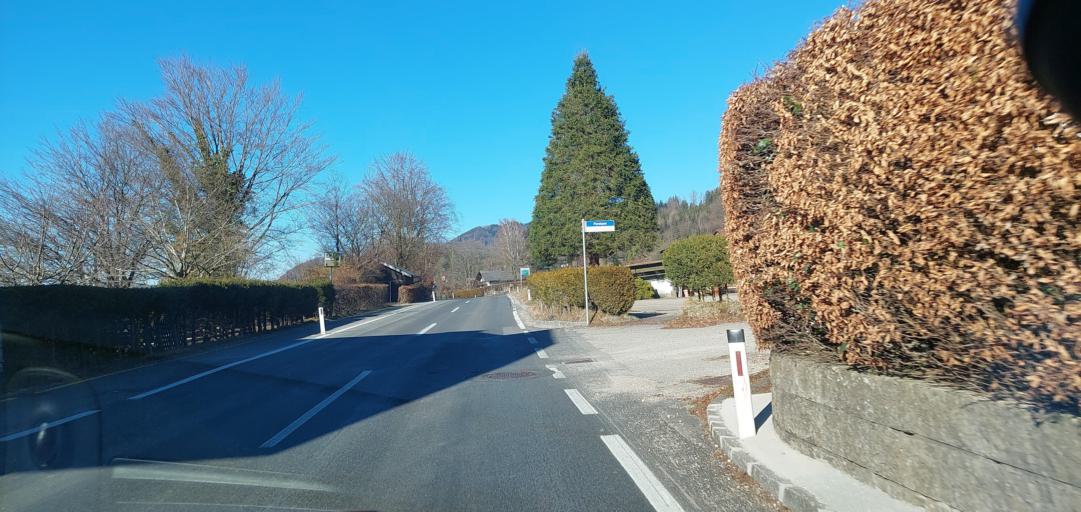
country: AT
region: Upper Austria
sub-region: Politischer Bezirk Vocklabruck
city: Steinbach am Attersee
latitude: 47.8157
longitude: 13.5466
